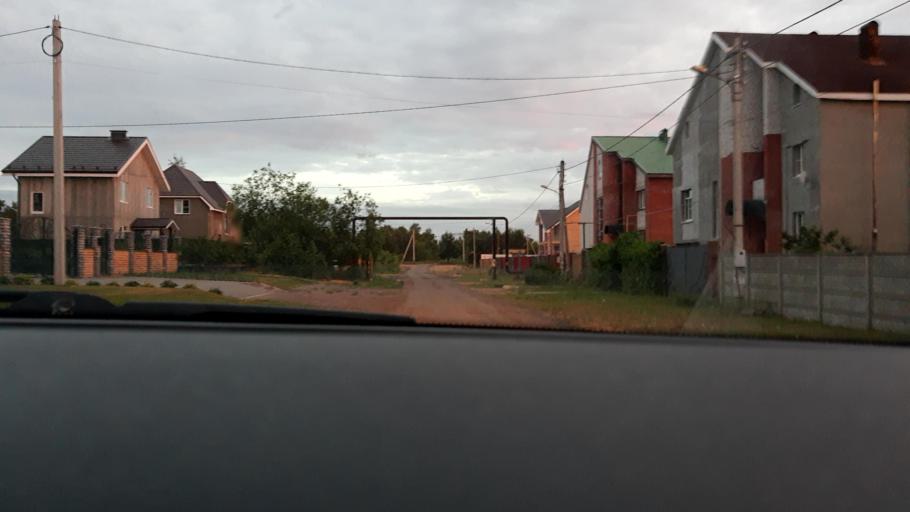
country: RU
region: Nizjnij Novgorod
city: Gorbatovka
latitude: 56.3844
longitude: 43.7656
